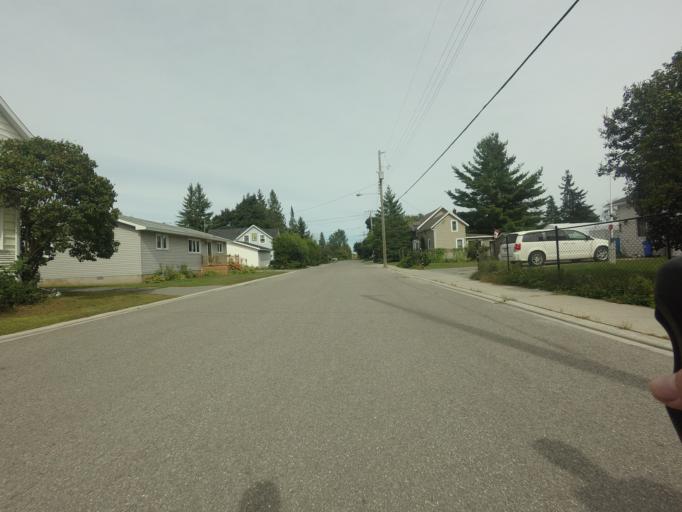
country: CA
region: Ontario
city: Carleton Place
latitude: 45.1393
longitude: -76.1363
